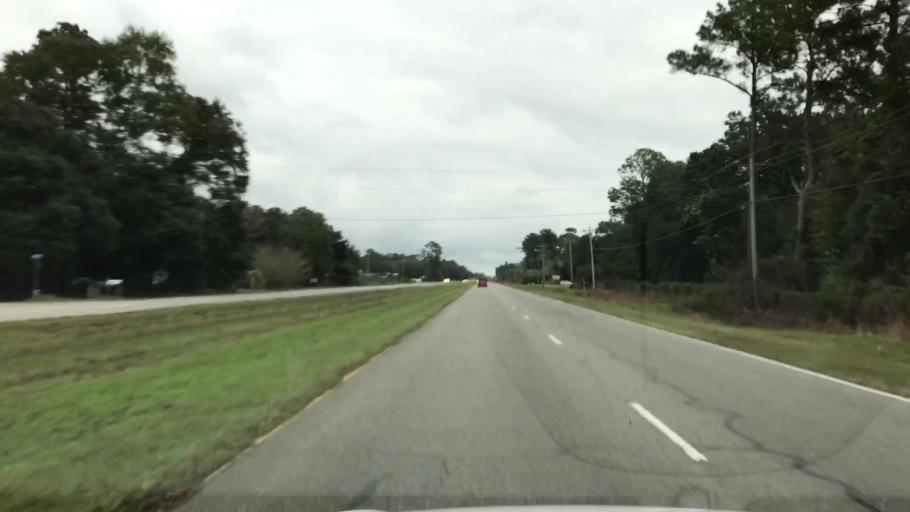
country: US
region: South Carolina
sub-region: Georgetown County
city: Georgetown
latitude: 33.3138
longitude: -79.3284
